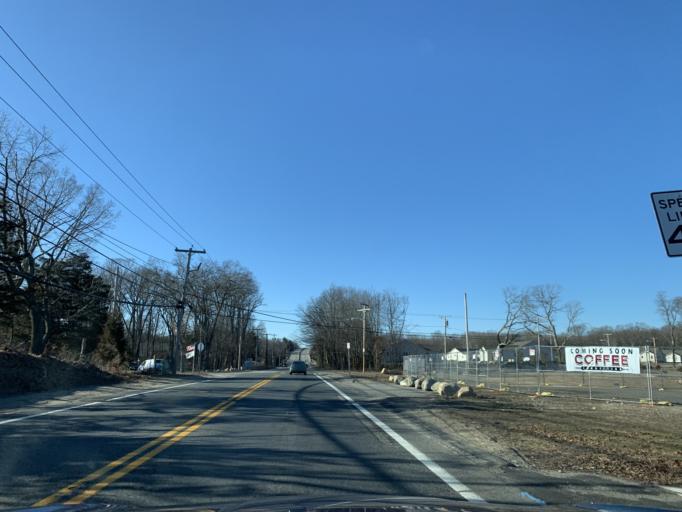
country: US
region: Rhode Island
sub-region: Providence County
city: Smithfield
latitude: 41.9030
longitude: -71.5056
